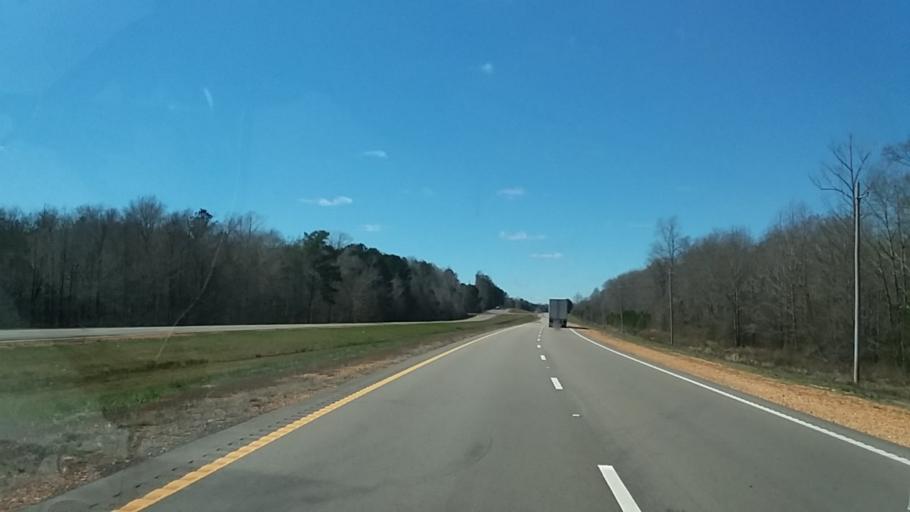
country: US
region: Mississippi
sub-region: Alcorn County
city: Farmington
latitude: 34.8572
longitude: -88.3893
